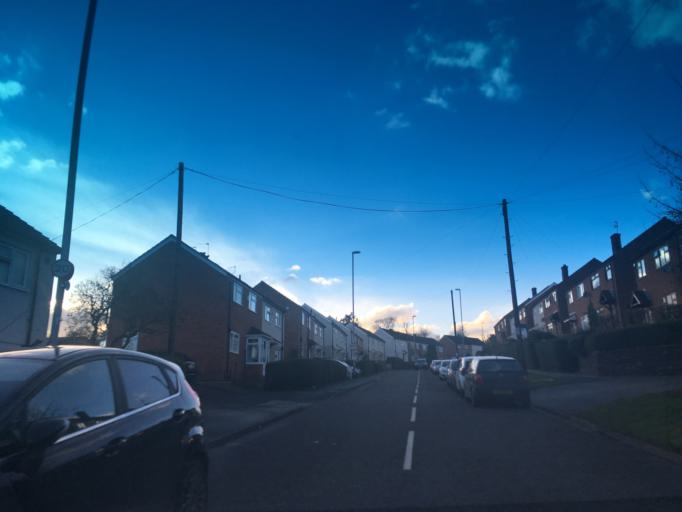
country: GB
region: England
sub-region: City and Borough of Leeds
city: Gildersome
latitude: 53.7850
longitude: -1.6165
